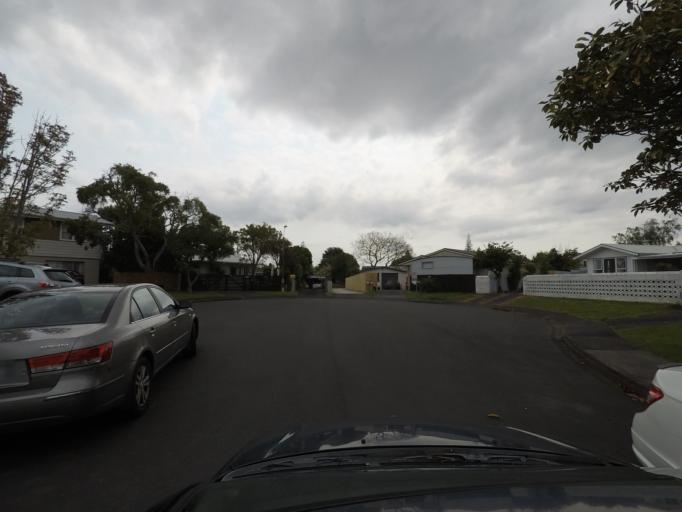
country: NZ
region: Auckland
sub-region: Auckland
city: Rosebank
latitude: -36.8453
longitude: 174.6492
